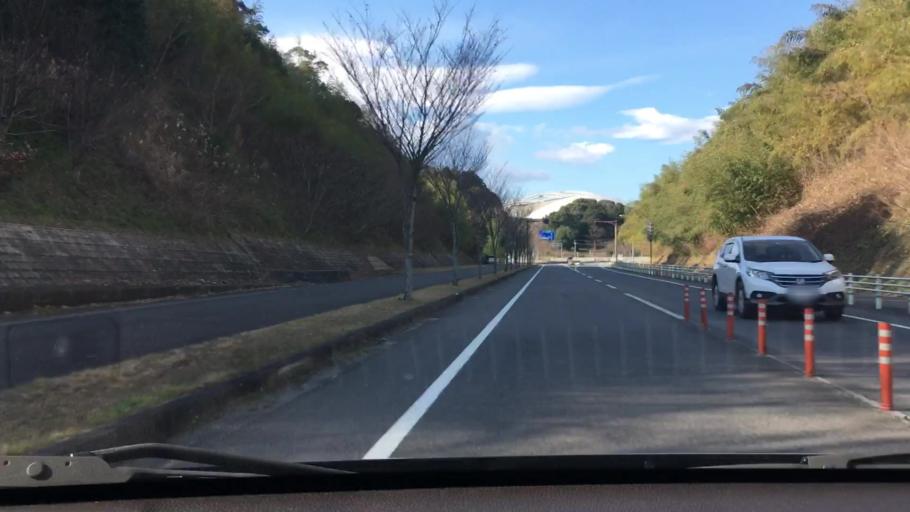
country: JP
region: Oita
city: Tsurusaki
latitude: 33.1929
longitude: 131.6671
